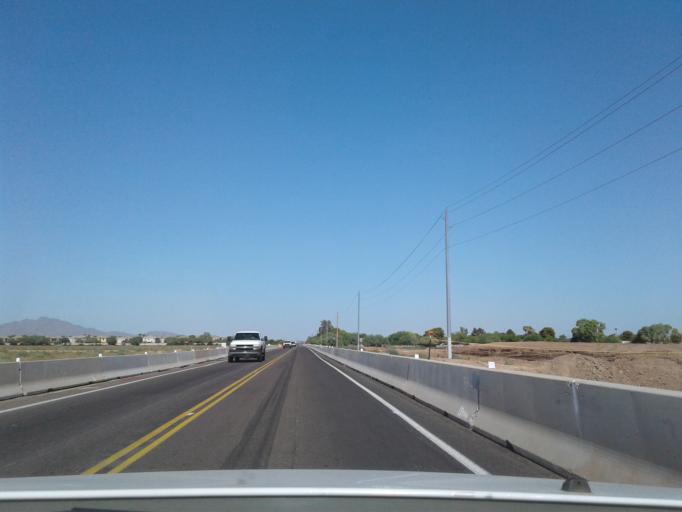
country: US
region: Arizona
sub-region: Maricopa County
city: Laveen
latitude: 33.3774
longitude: -112.1888
